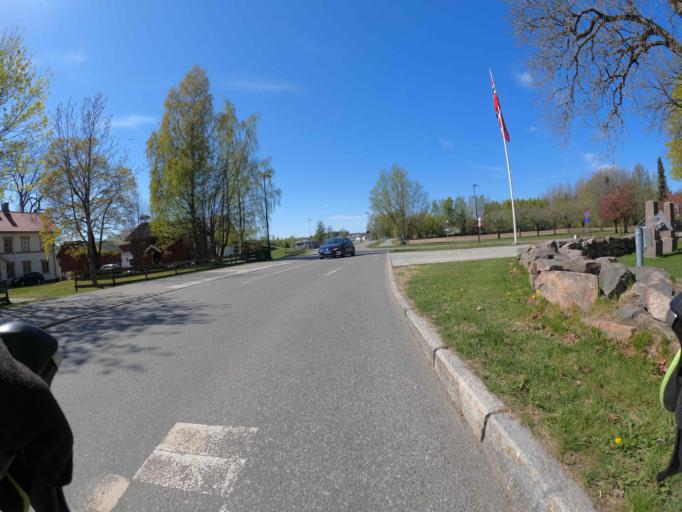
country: NO
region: Akershus
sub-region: Skedsmo
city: Lillestrom
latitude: 59.9936
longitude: 11.0448
